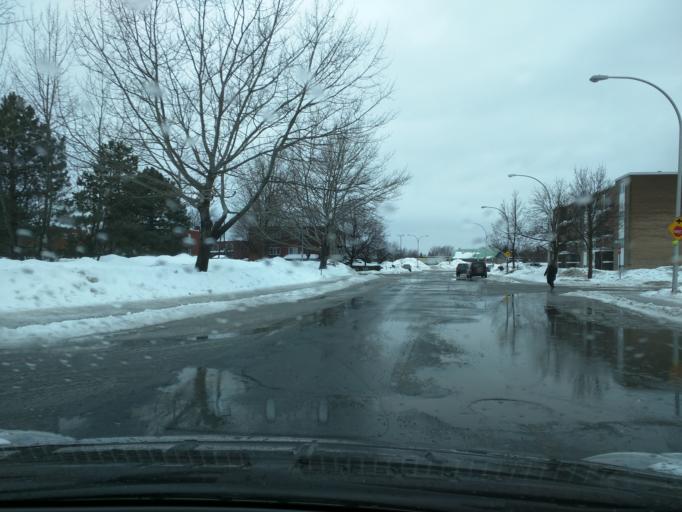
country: CA
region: Quebec
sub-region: Monteregie
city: Longueuil
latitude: 45.5239
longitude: -73.4582
